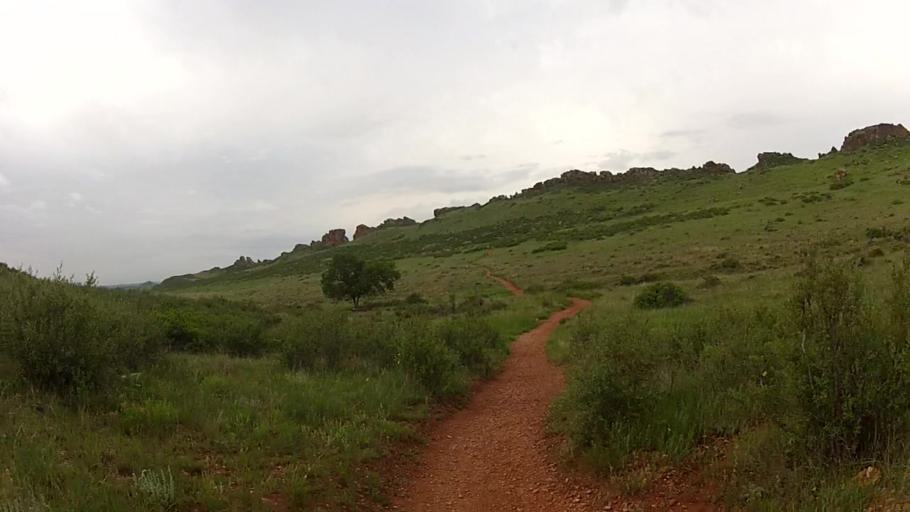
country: US
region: Colorado
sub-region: Larimer County
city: Loveland
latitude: 40.4283
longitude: -105.1629
